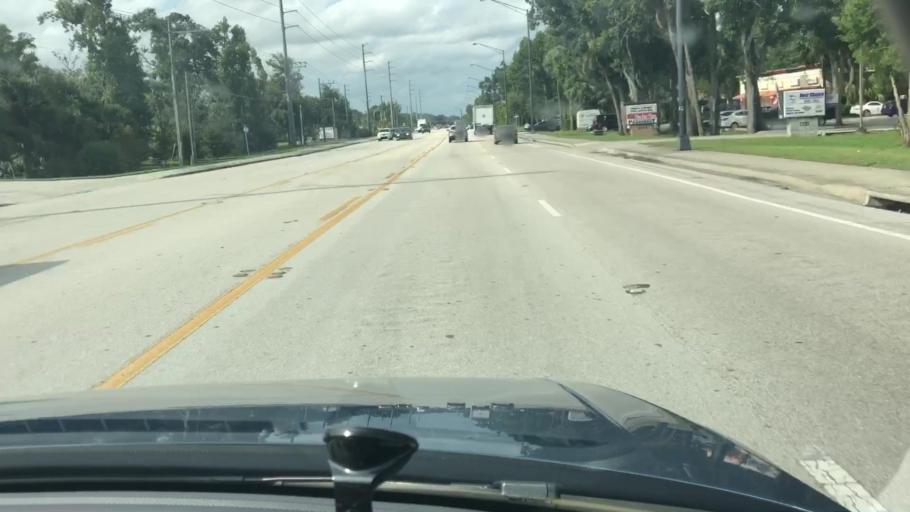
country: US
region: Florida
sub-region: Volusia County
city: Port Orange
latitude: 29.1312
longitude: -81.0070
